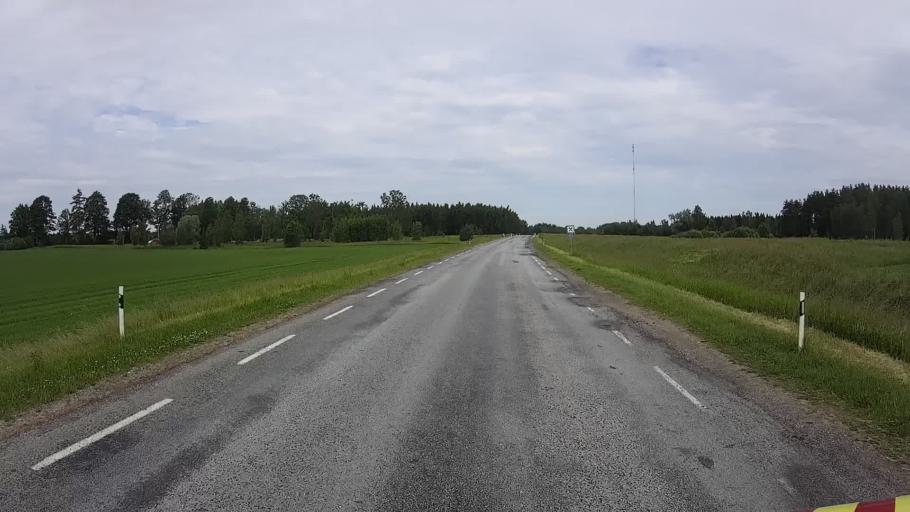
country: EE
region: Viljandimaa
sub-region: Viljandi linn
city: Viljandi
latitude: 58.2310
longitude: 25.6021
